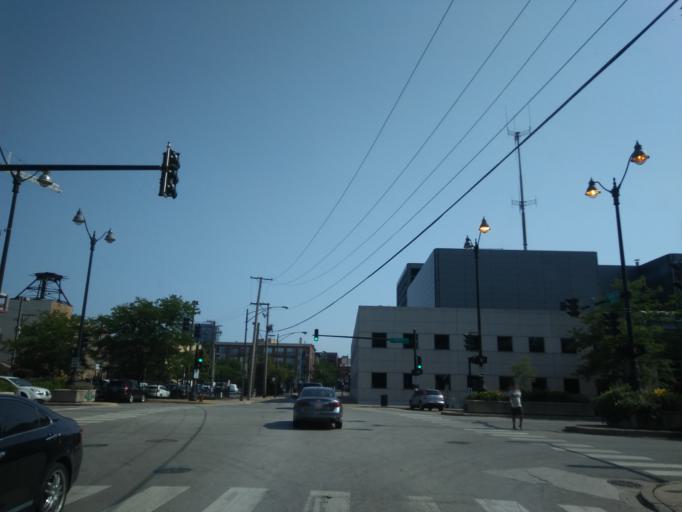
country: US
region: Illinois
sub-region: Cook County
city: Chicago
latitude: 41.8844
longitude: -87.6567
